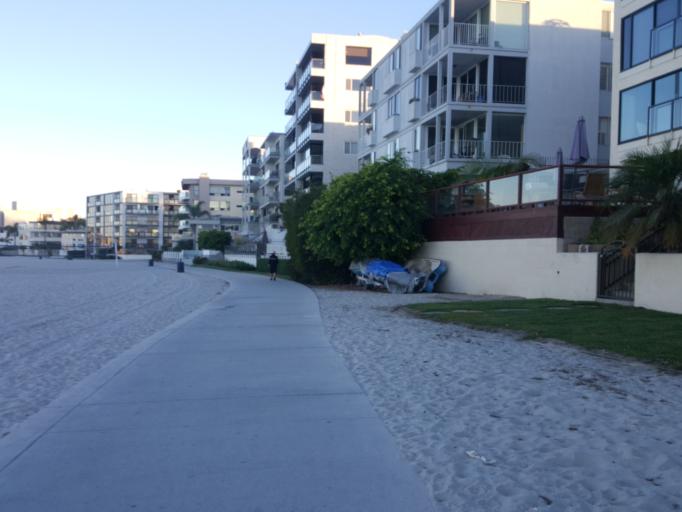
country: US
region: California
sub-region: San Diego County
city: La Jolla
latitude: 32.7885
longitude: -117.2409
